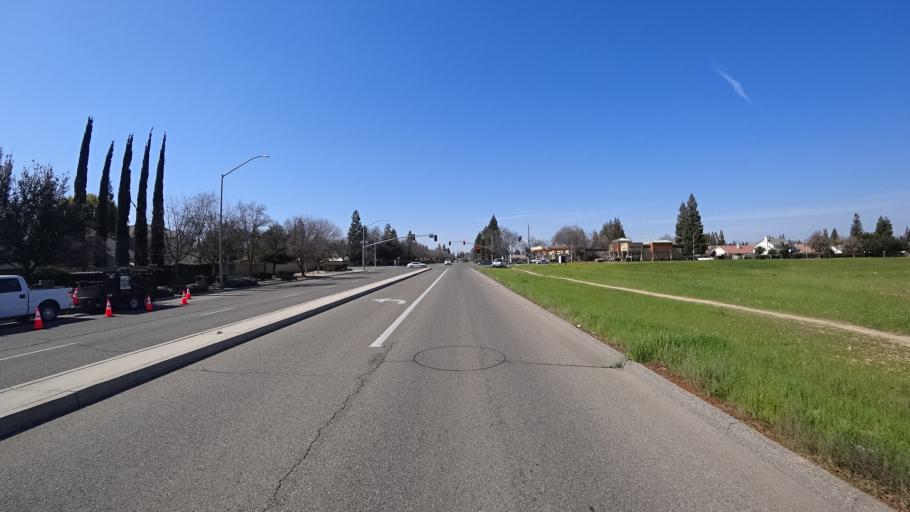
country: US
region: California
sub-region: Fresno County
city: Clovis
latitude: 36.8812
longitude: -119.7466
